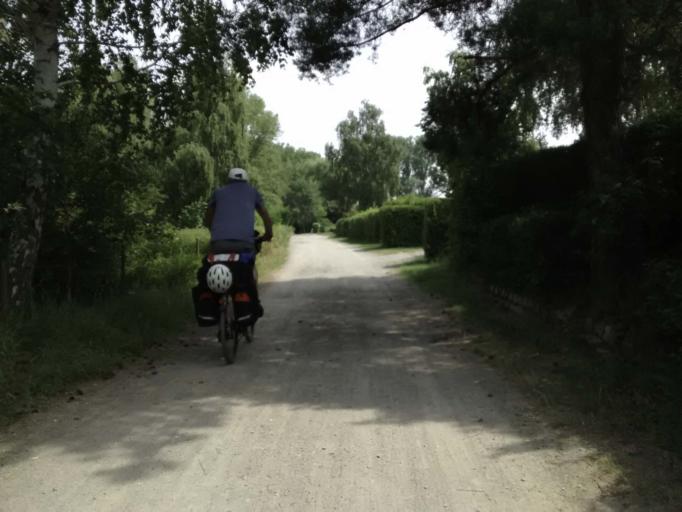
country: DE
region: Saxony-Anhalt
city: Magdeburg
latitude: 52.0996
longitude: 11.6642
